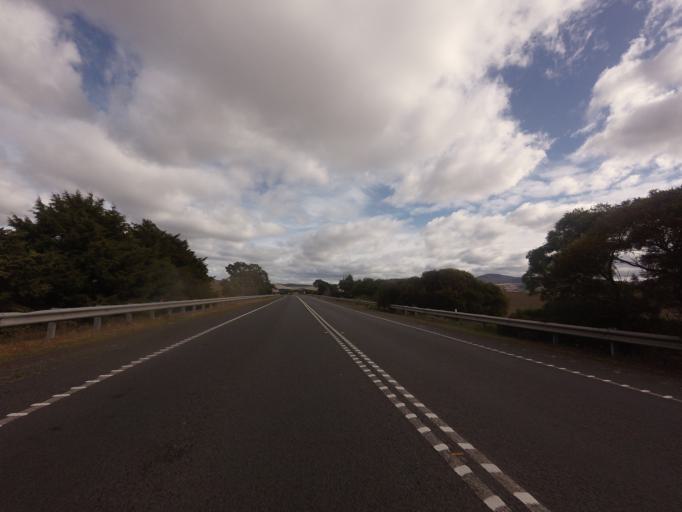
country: AU
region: Tasmania
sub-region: Brighton
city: Bridgewater
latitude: -42.4646
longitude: 147.1871
